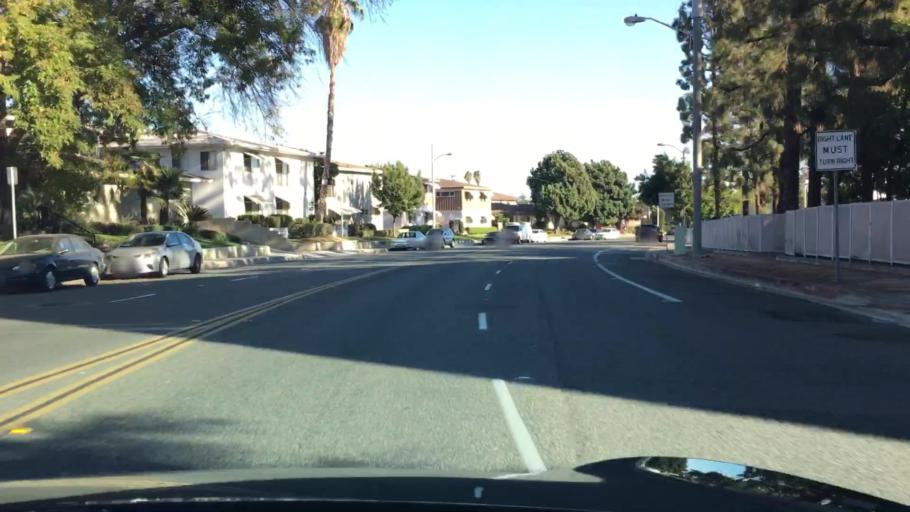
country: US
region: California
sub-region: Los Angeles County
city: Temple City
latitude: 34.1337
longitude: -118.0663
